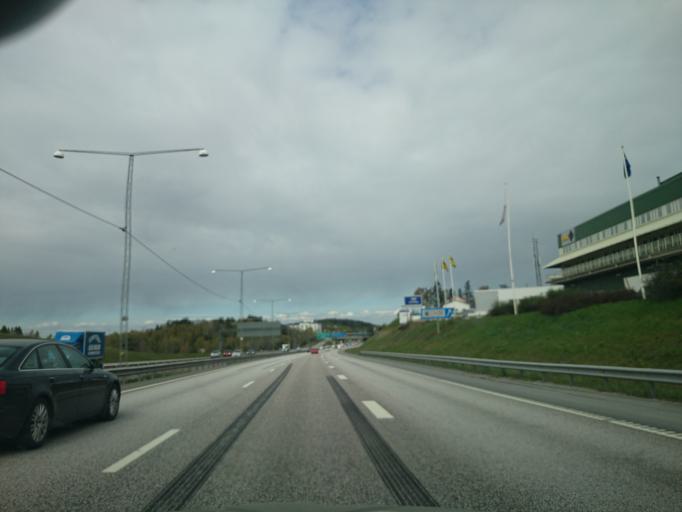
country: SE
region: Stockholm
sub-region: Upplands Vasby Kommun
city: Upplands Vaesby
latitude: 59.5076
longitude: 17.9246
